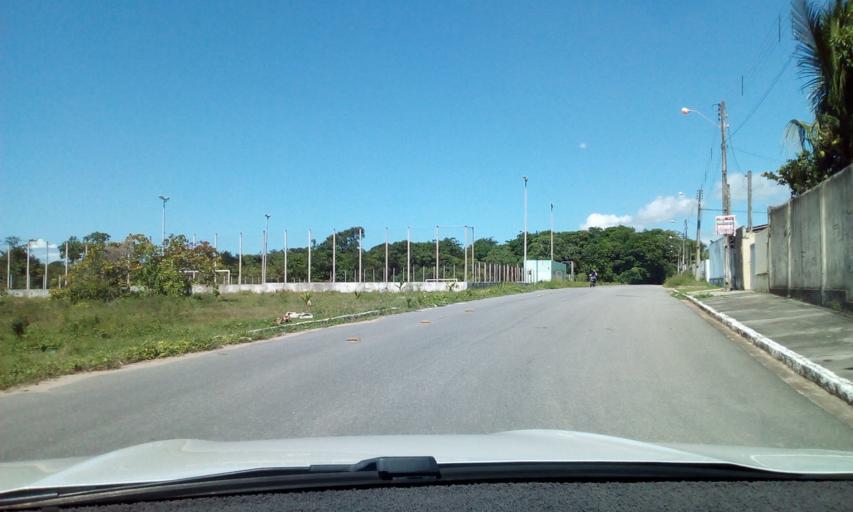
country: BR
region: Paraiba
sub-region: Joao Pessoa
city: Joao Pessoa
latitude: -7.1792
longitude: -34.8239
